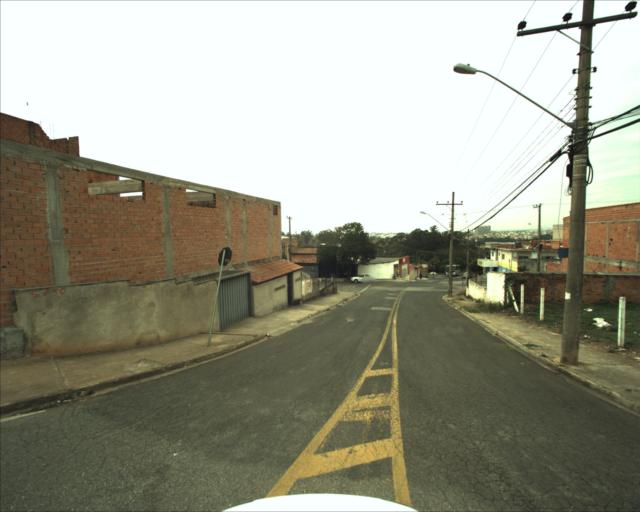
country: BR
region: Sao Paulo
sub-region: Sorocaba
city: Sorocaba
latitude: -23.4956
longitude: -47.5299
